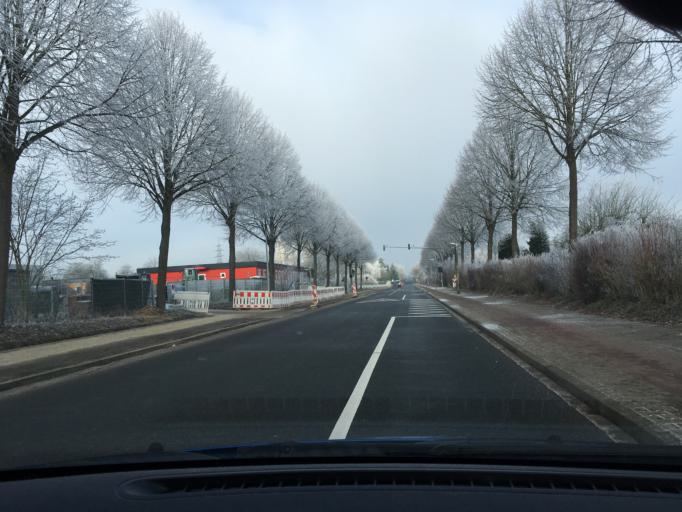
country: DE
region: Lower Saxony
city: Lueneburg
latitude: 53.2628
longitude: 10.3907
